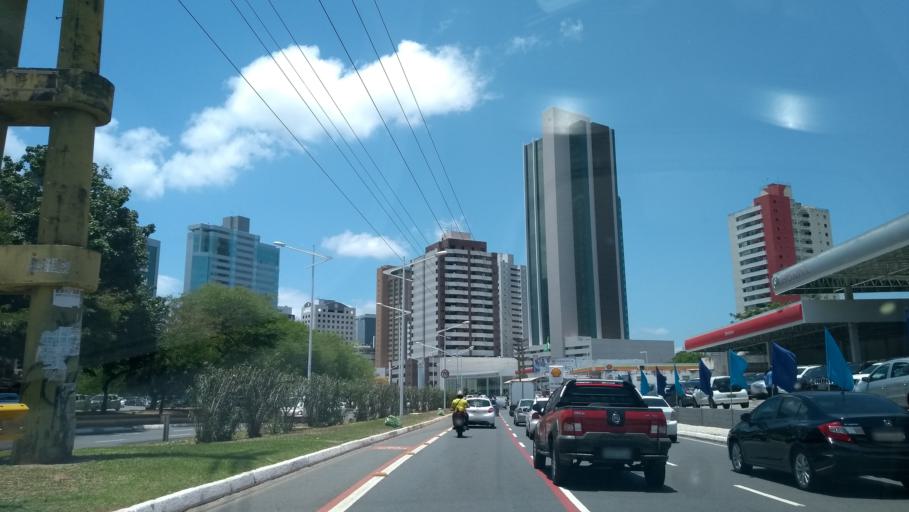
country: BR
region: Bahia
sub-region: Salvador
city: Salvador
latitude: -12.9899
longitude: -38.4499
